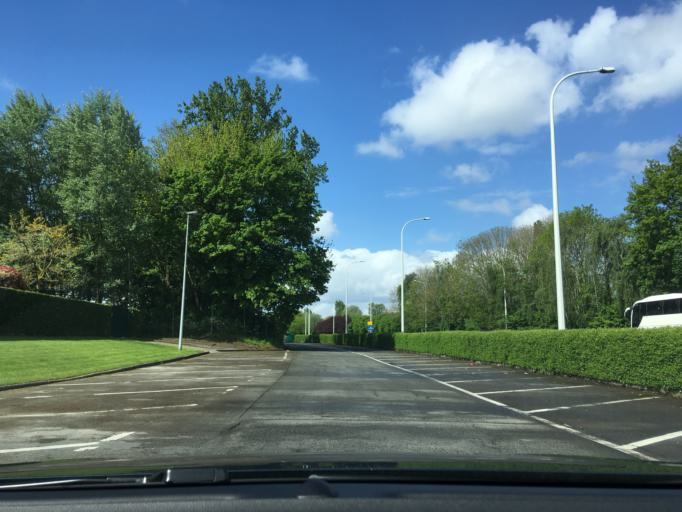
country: BE
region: Flanders
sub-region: Provincie West-Vlaanderen
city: Tielt
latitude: 51.0056
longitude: 3.3316
